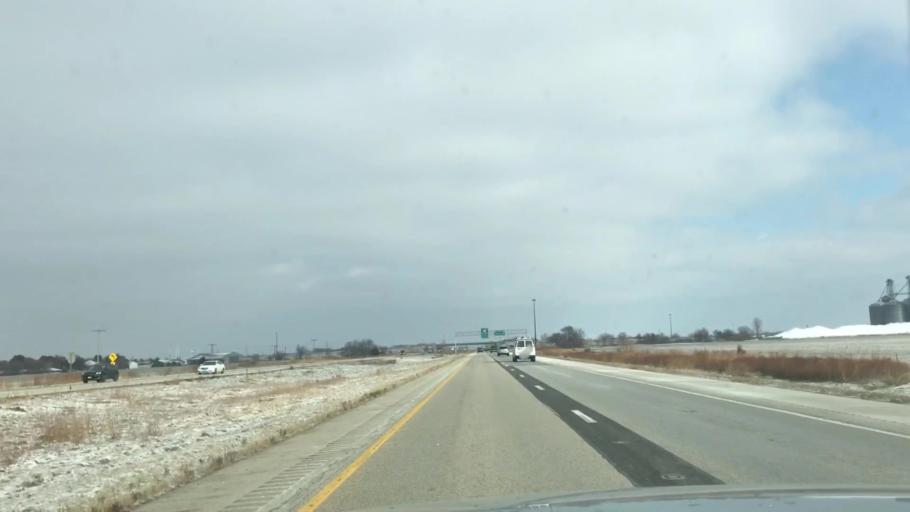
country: US
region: Illinois
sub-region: Sangamon County
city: Divernon
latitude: 39.5598
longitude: -89.6458
